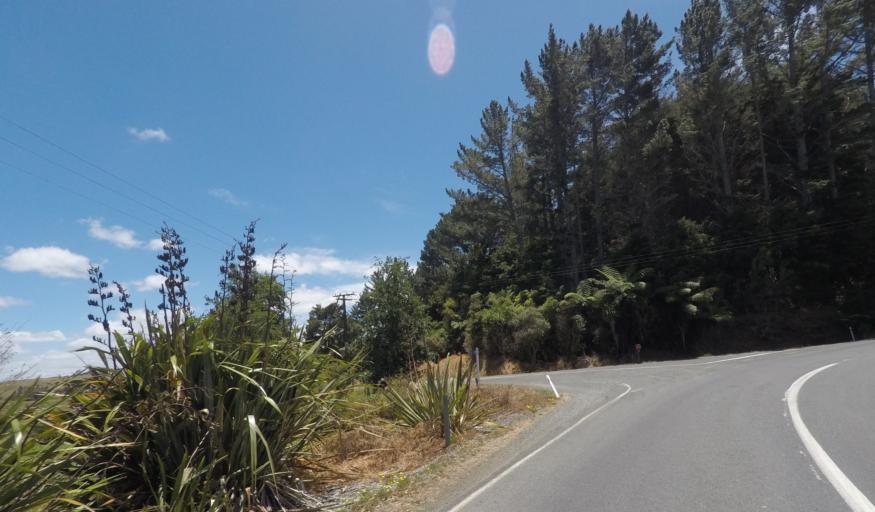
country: NZ
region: Northland
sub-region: Whangarei
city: Whangarei
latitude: -35.5458
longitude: 174.3049
